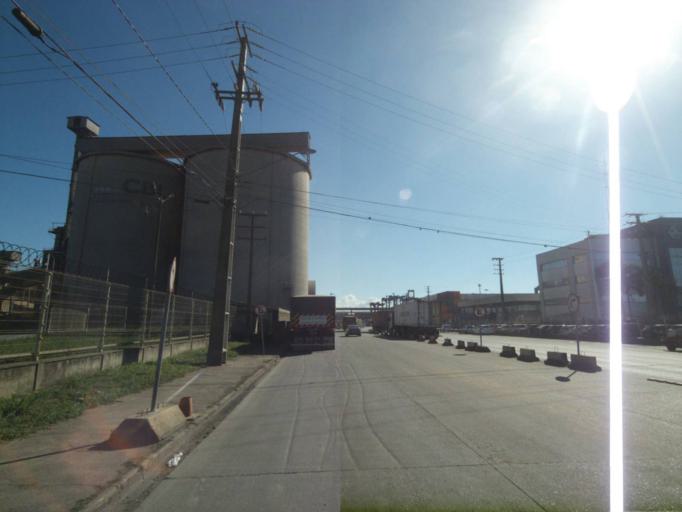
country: BR
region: Parana
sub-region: Paranagua
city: Paranagua
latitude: -25.5053
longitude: -48.5041
